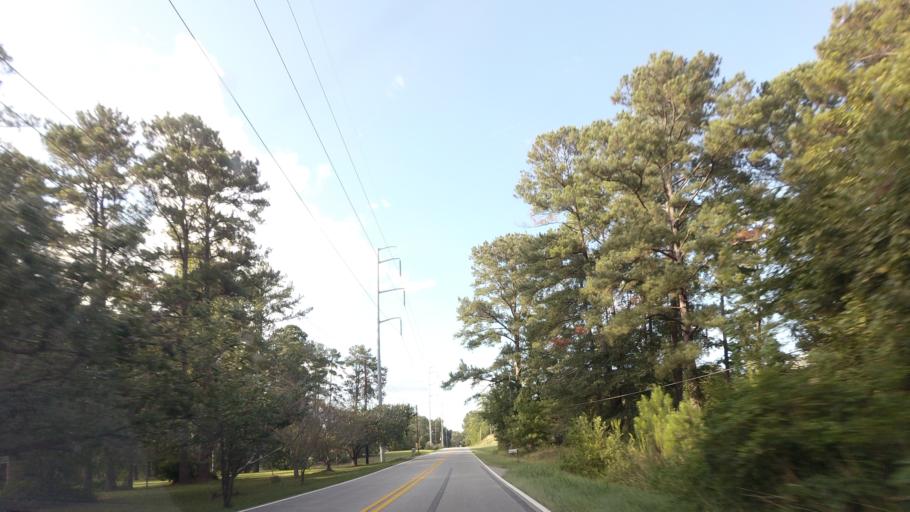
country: US
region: Georgia
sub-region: Bibb County
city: West Point
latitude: 32.8415
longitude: -83.7451
